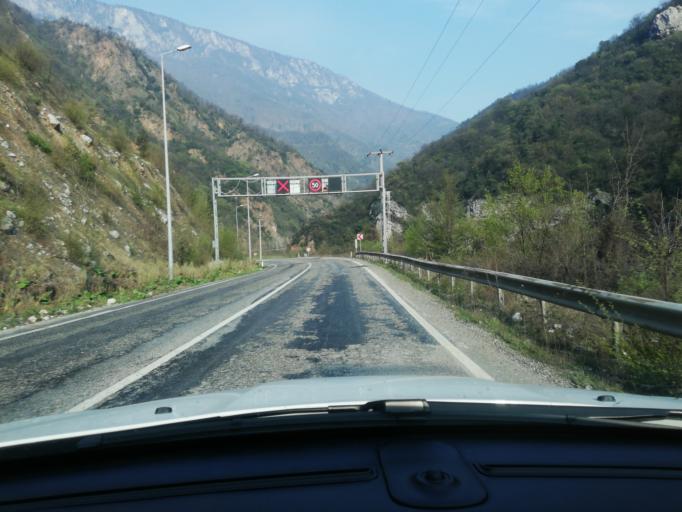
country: TR
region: Karabuk
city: Yenice
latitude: 41.1580
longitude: 32.4644
